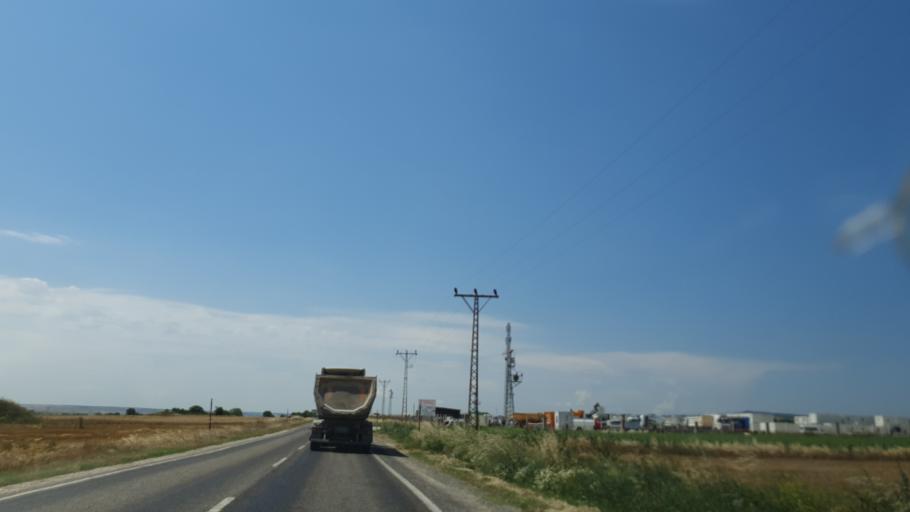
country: TR
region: Tekirdag
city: Saray
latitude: 41.5181
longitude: 27.8613
